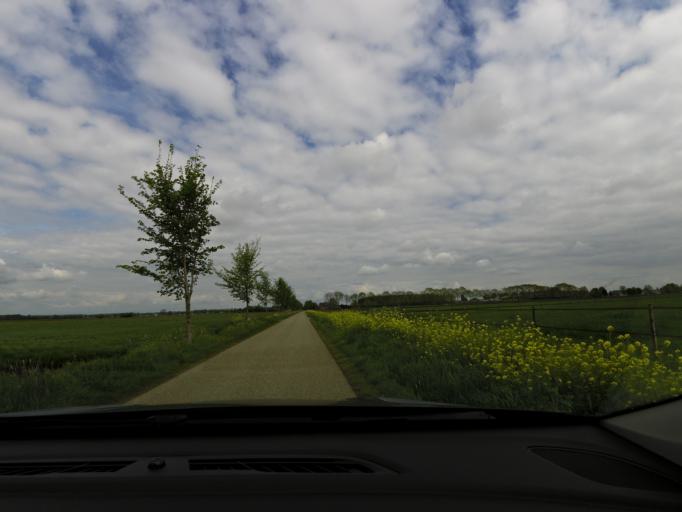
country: NL
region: Gelderland
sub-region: Gemeente Buren
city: Lienden
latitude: 51.9335
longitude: 5.4664
